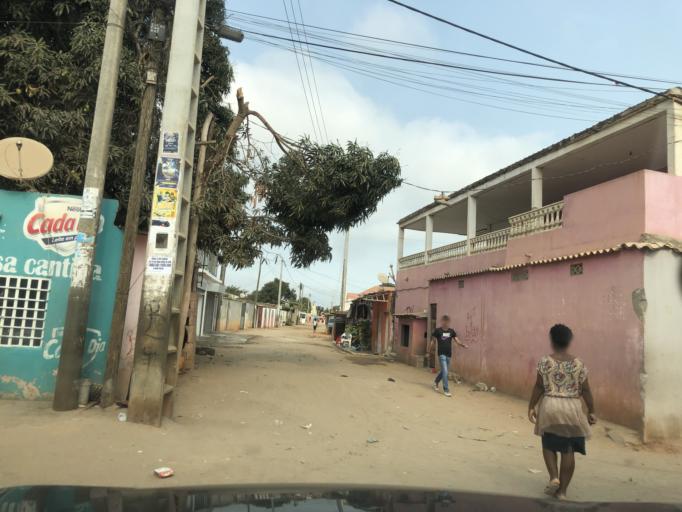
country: AO
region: Luanda
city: Luanda
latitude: -8.9177
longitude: 13.1731
